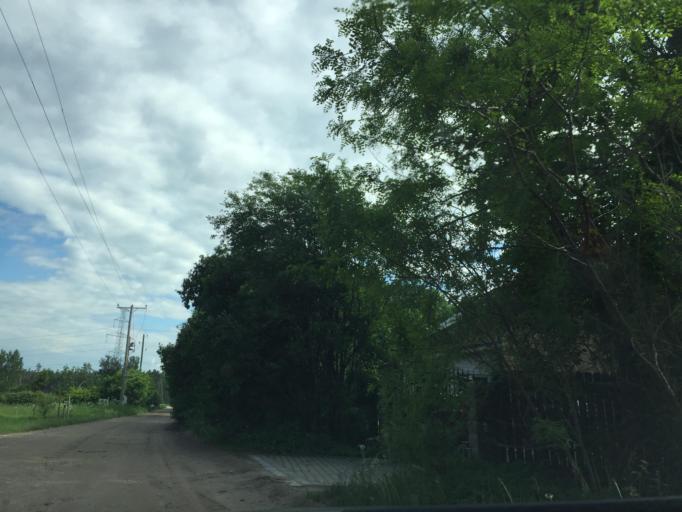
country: LV
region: Stopini
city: Ulbroka
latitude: 56.9283
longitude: 24.2896
